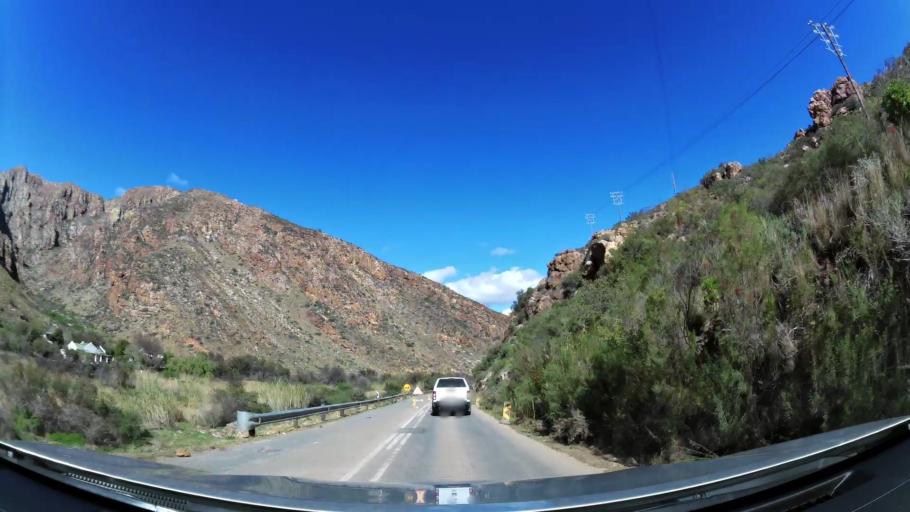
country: ZA
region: Western Cape
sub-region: Cape Winelands District Municipality
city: Ashton
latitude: -33.8099
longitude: 20.0937
